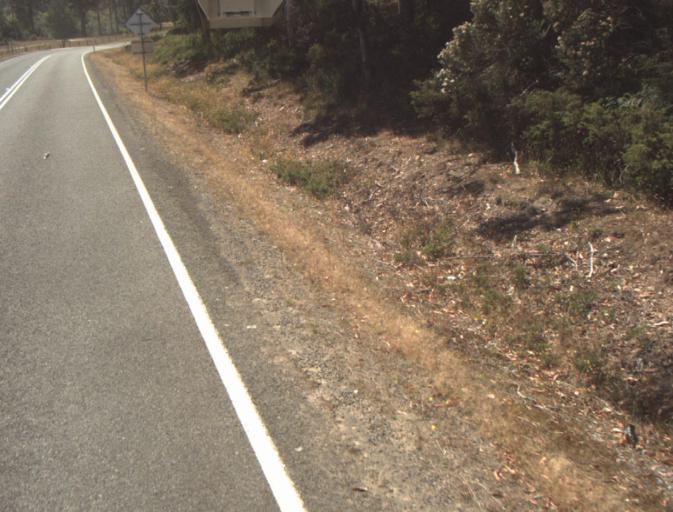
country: AU
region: Tasmania
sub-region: Dorset
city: Scottsdale
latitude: -41.3030
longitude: 147.3817
